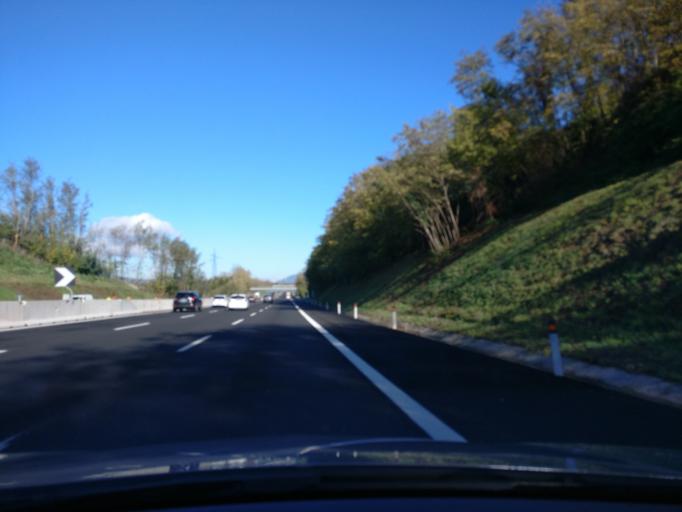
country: IT
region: Campania
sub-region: Provincia di Caserta
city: Zuni
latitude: 41.2207
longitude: 14.0983
